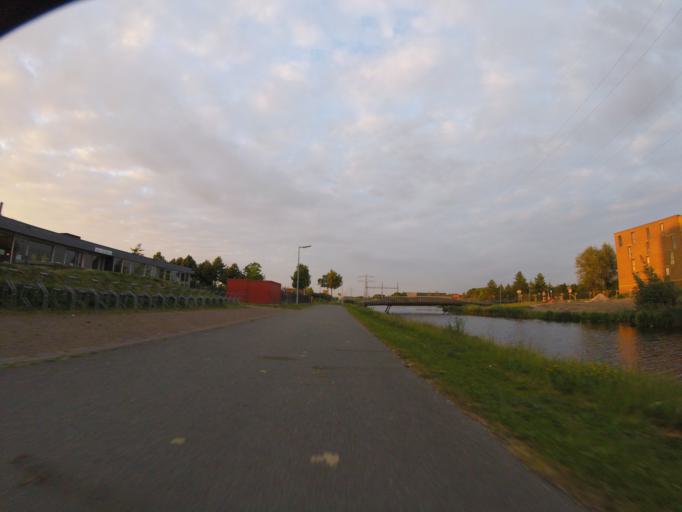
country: NL
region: North Holland
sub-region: Gemeente Bloemendaal
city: Bennebroek
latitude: 52.3102
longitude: 4.6395
